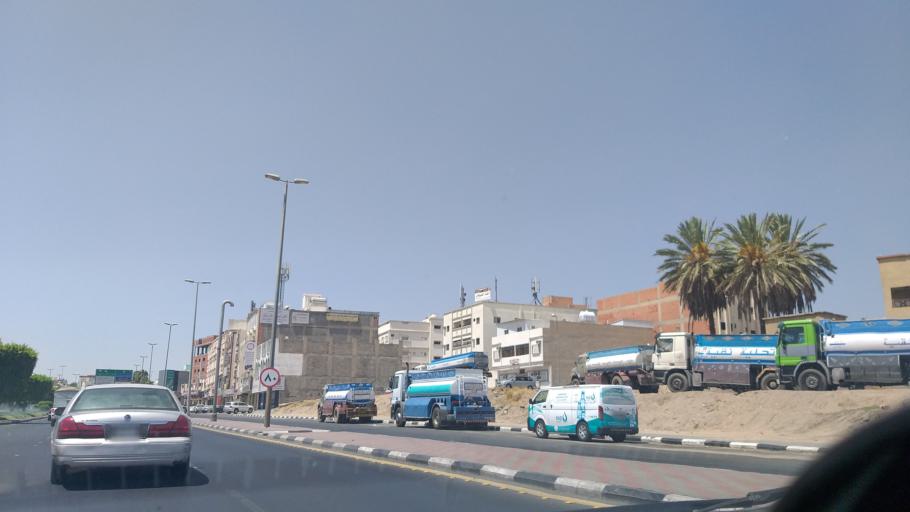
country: SA
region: Makkah
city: Ta'if
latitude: 21.2779
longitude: 40.4234
